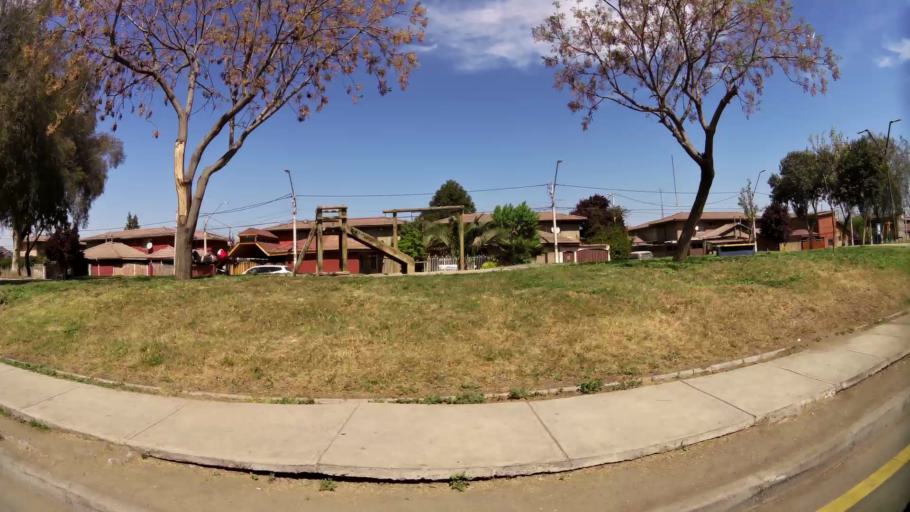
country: CL
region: Santiago Metropolitan
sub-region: Provincia de Santiago
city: Lo Prado
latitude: -33.3976
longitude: -70.7442
